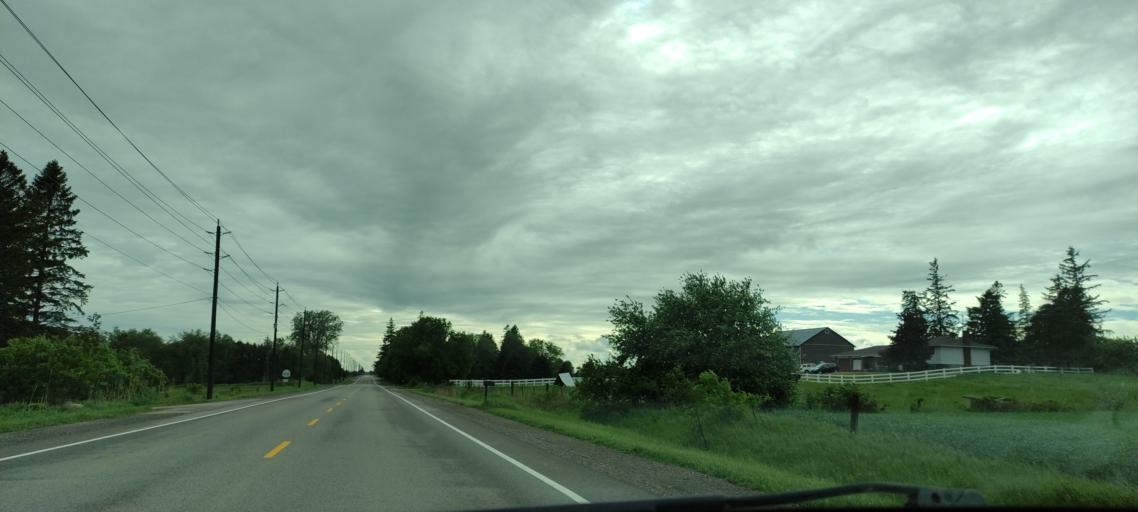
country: CA
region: Ontario
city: Kitchener
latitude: 43.3849
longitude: -80.6328
